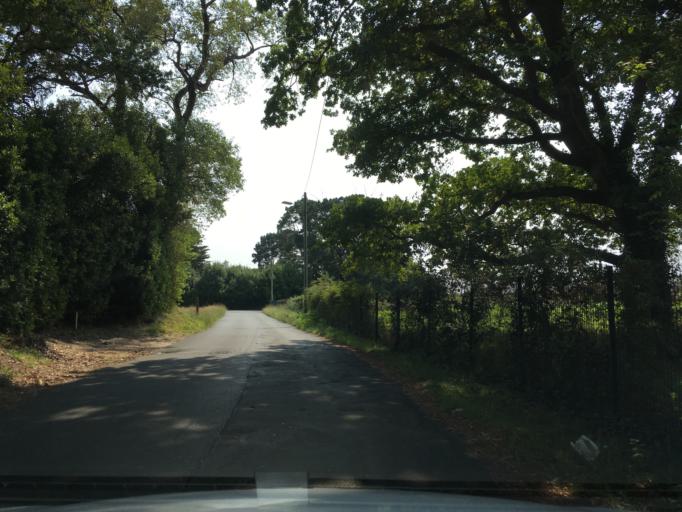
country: FR
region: Aquitaine
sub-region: Departement des Pyrenees-Atlantiques
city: Anglet
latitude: 43.5013
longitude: -1.5211
